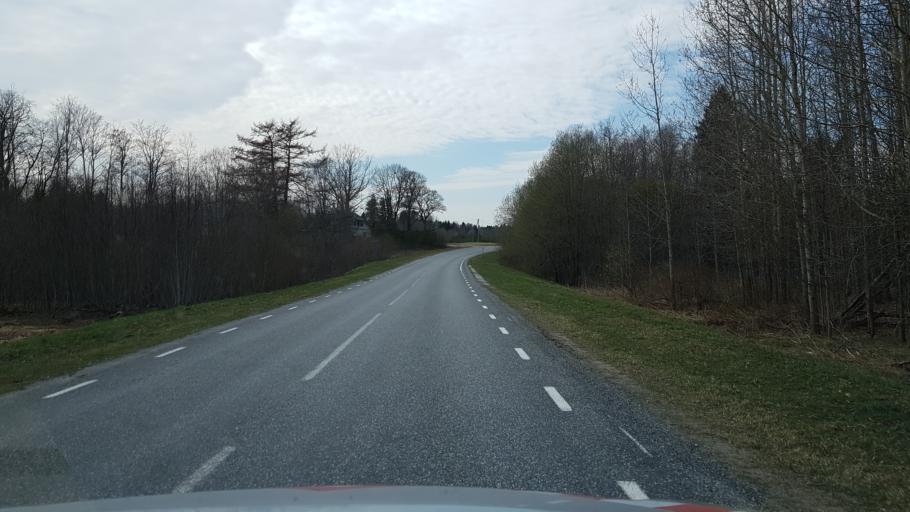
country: EE
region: Laeaene-Virumaa
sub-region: Haljala vald
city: Haljala
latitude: 59.4639
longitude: 26.1894
